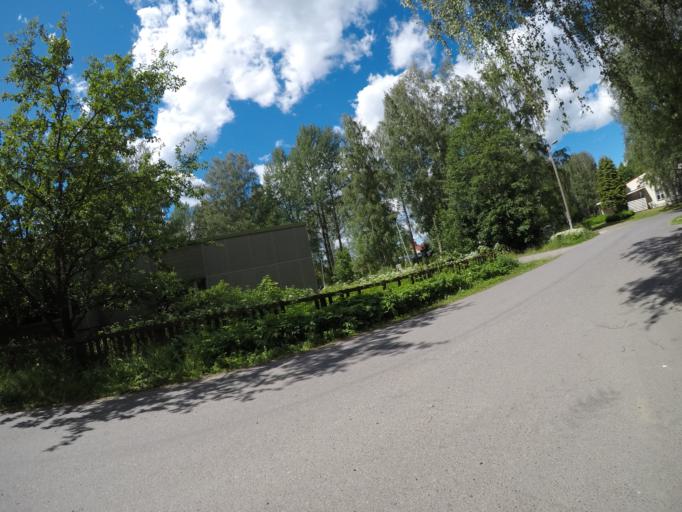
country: FI
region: Haeme
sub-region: Haemeenlinna
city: Haemeenlinna
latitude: 61.0097
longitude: 24.4374
